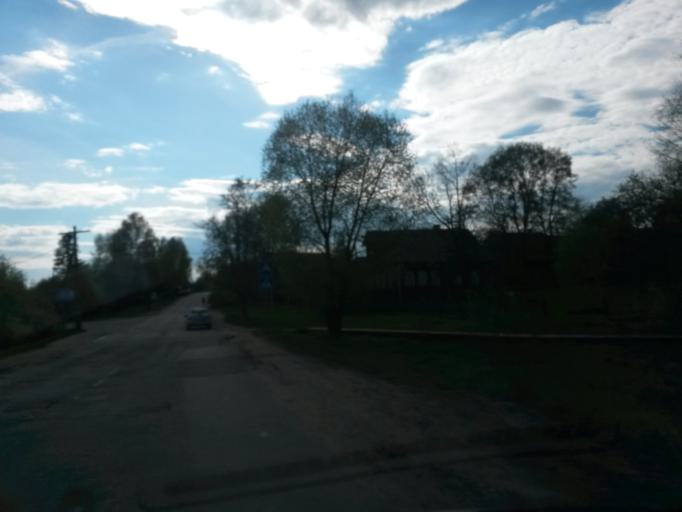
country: RU
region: Jaroslavl
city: Myshkin
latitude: 57.7808
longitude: 38.4482
